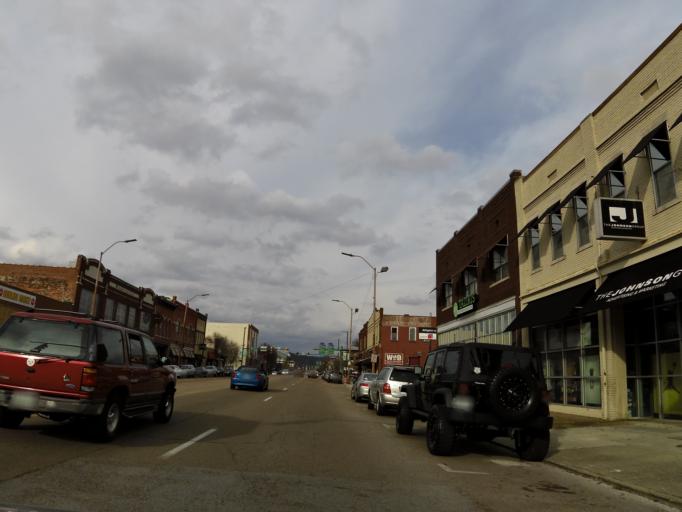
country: US
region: Tennessee
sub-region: Hamilton County
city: Chattanooga
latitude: 35.0509
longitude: -85.3095
